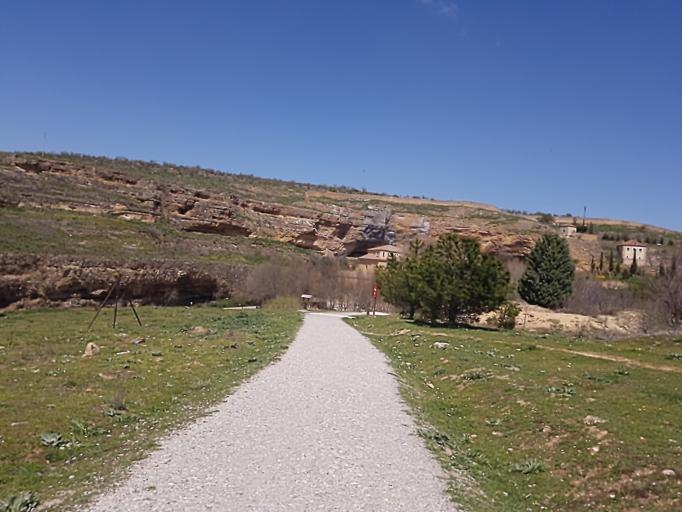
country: ES
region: Castille and Leon
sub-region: Provincia de Segovia
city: Segovia
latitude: 40.9546
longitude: -4.1359
